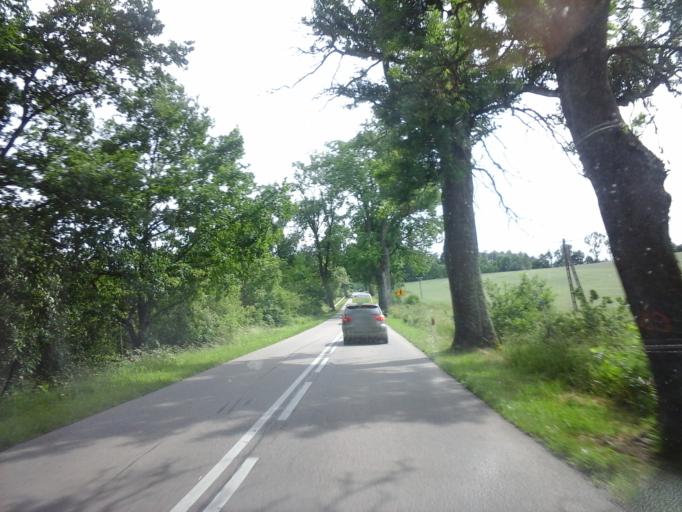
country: PL
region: West Pomeranian Voivodeship
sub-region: Powiat lobeski
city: Wegorzyno
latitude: 53.5739
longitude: 15.5879
